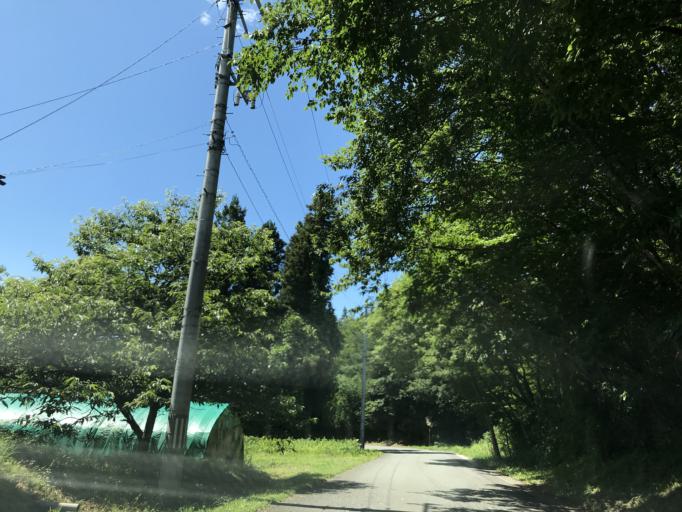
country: JP
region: Iwate
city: Ichinoseki
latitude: 38.9354
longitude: 141.0256
